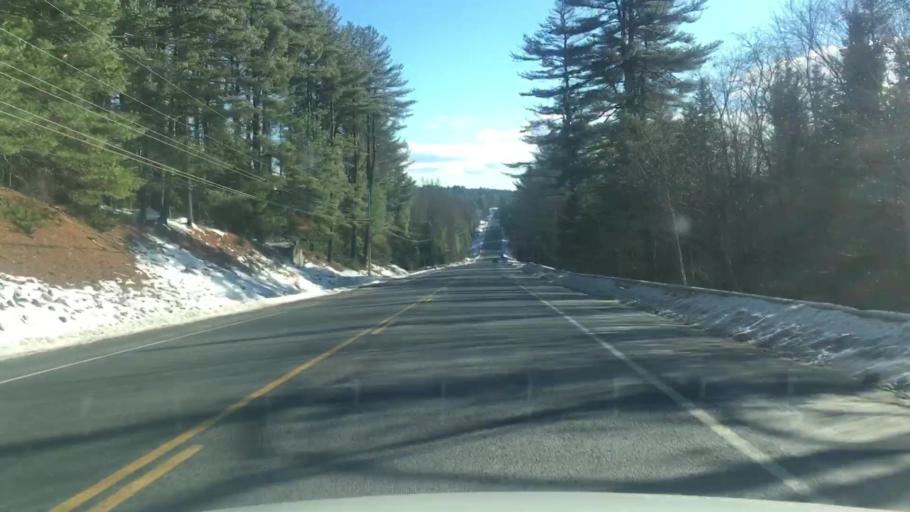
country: US
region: Maine
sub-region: Somerset County
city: Madison
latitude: 44.9327
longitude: -69.8364
